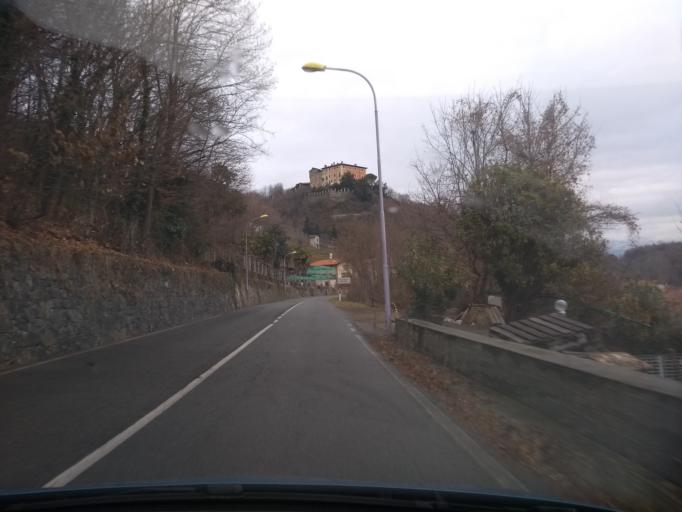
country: IT
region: Piedmont
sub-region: Provincia di Torino
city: Colleretto Giacosa
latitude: 45.4320
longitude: 7.7966
